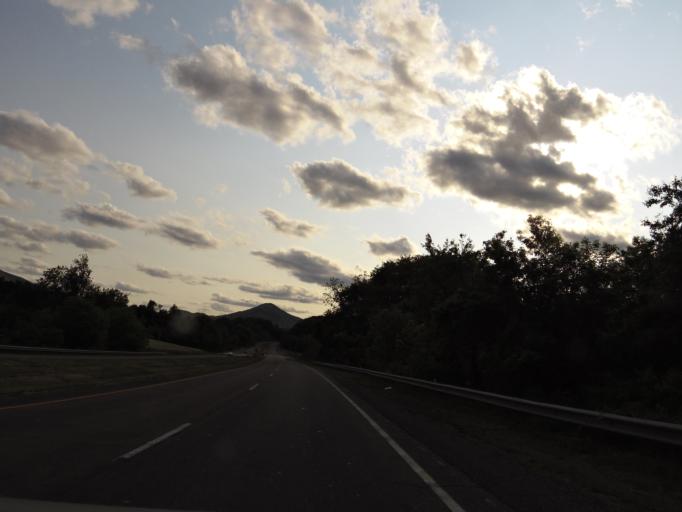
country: US
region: Virginia
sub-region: Tazewell County
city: Tazewell
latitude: 37.1234
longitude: -81.5418
